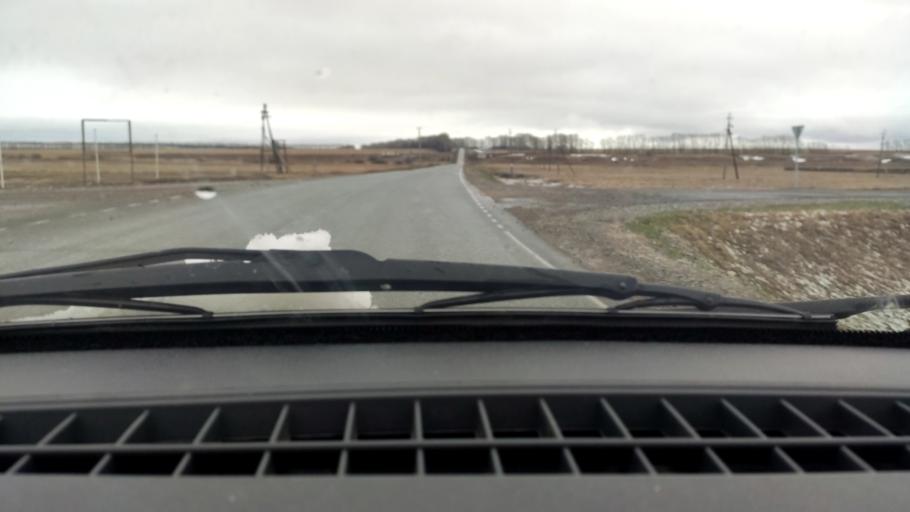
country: RU
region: Bashkortostan
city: Alekseyevka
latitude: 55.0724
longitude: 55.0855
